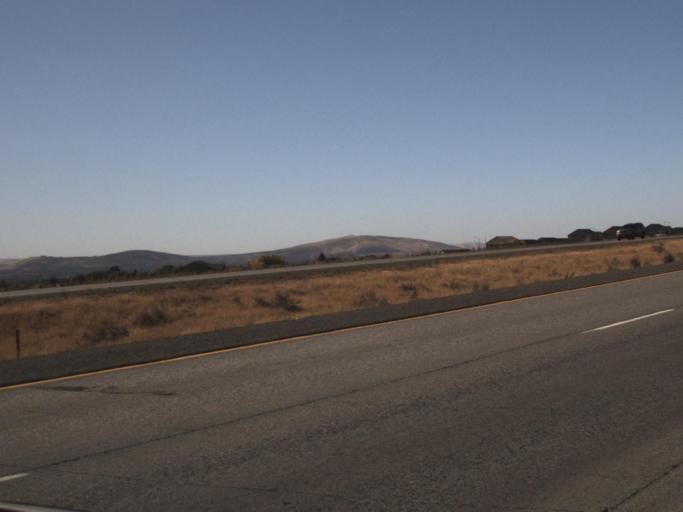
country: US
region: Washington
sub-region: Franklin County
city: West Pasco
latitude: 46.2584
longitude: -119.1584
